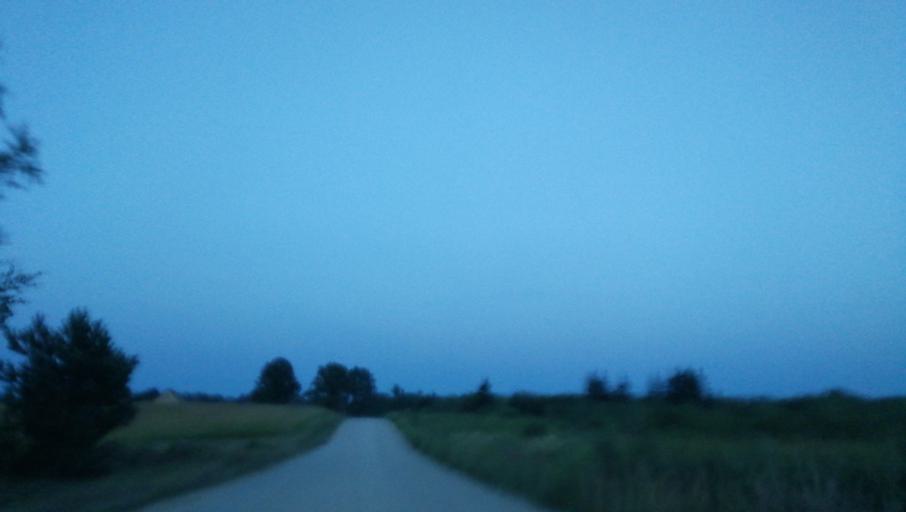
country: LV
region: Amatas Novads
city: Drabesi
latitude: 57.2469
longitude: 25.1942
